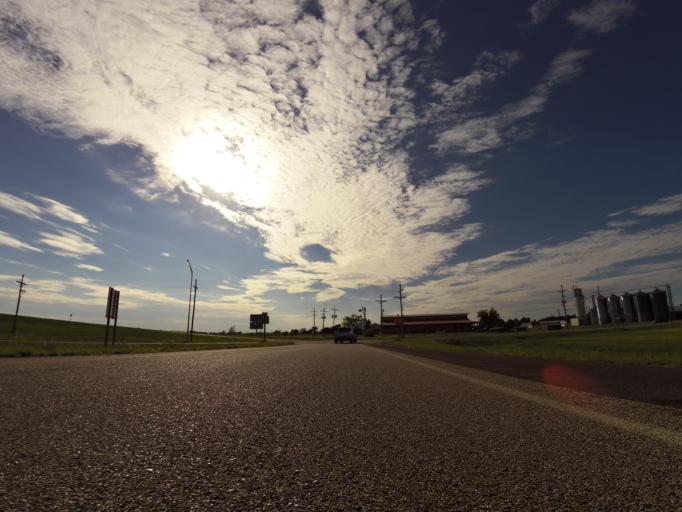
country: US
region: Kansas
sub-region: Reno County
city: Haven
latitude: 37.9370
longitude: -97.8662
